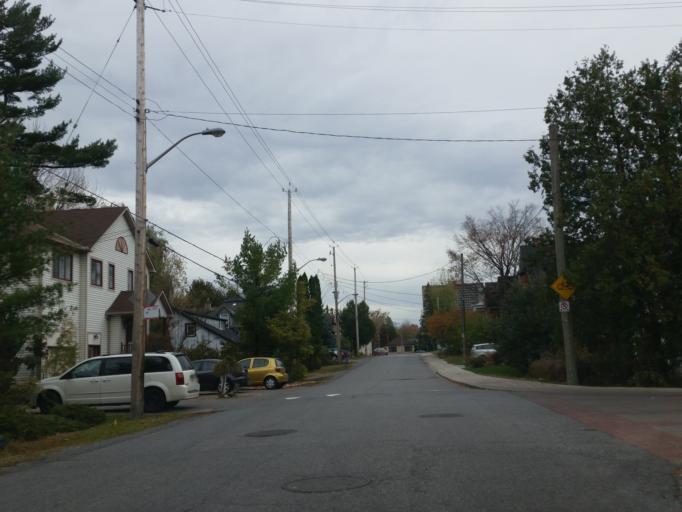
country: CA
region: Ontario
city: Bells Corners
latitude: 45.3669
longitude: -75.7976
